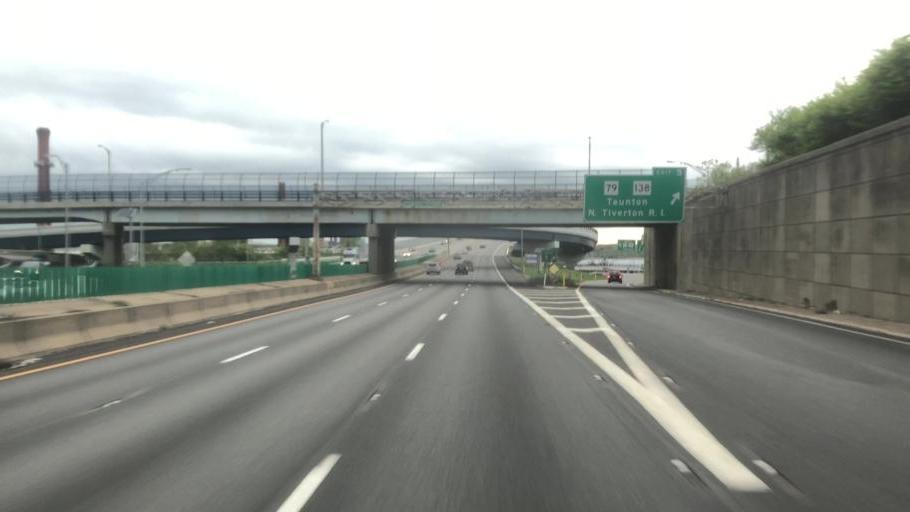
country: US
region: Massachusetts
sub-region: Bristol County
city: Fall River
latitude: 41.7018
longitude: -71.1558
